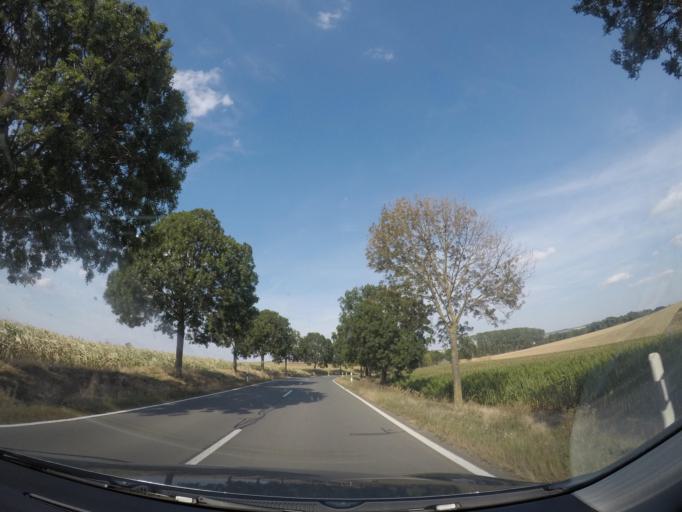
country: DE
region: Saxony-Anhalt
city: Langeln
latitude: 51.9397
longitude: 10.8145
